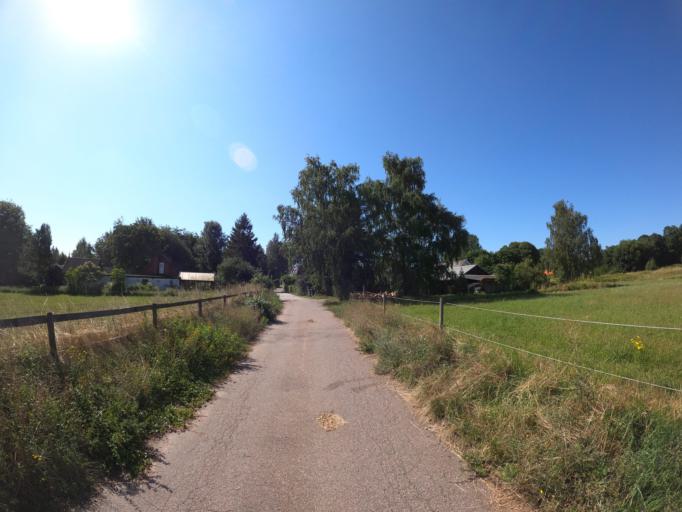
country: SE
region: Skane
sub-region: Lunds Kommun
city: Veberod
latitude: 55.6776
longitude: 13.4250
